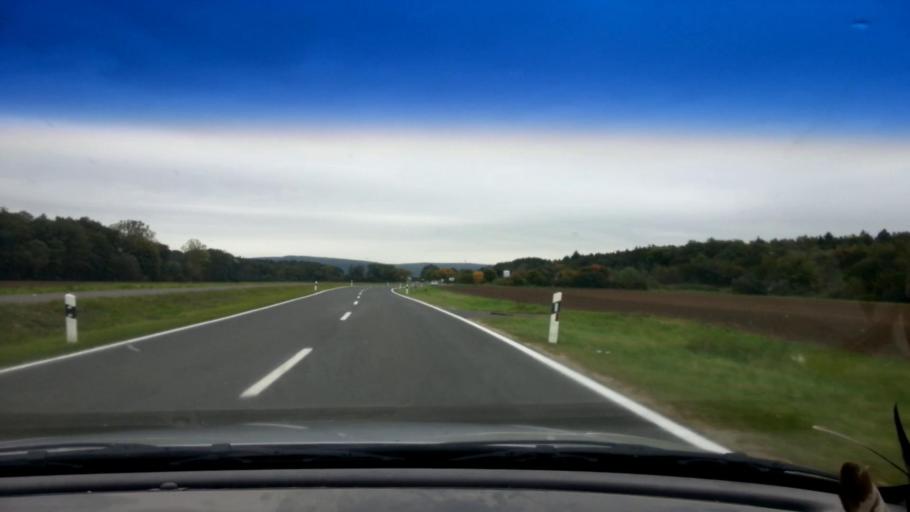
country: DE
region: Bavaria
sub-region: Upper Franconia
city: Memmelsdorf
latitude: 49.9204
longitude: 10.9659
